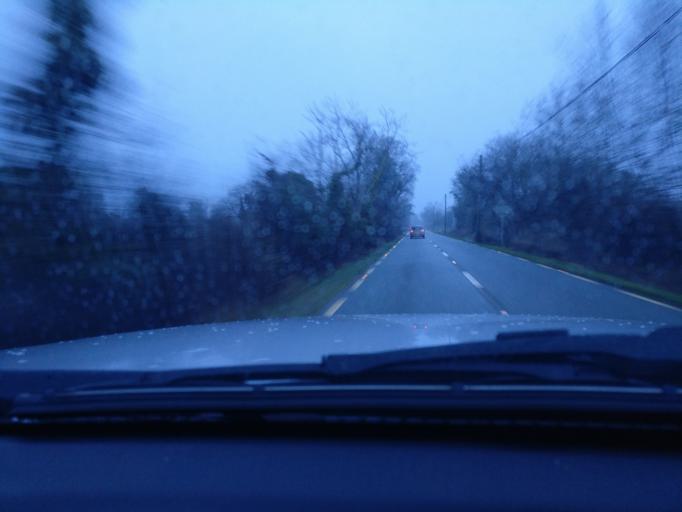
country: IE
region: Leinster
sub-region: An Mhi
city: Athboy
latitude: 53.6421
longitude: -6.8418
